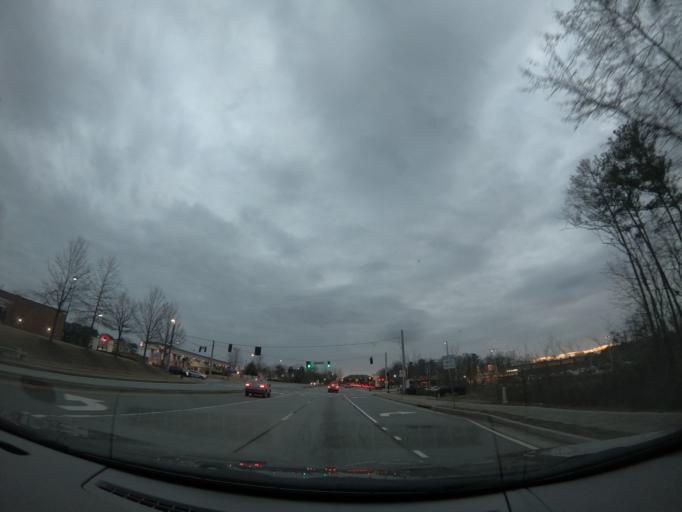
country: US
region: Georgia
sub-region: Fulton County
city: Roswell
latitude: 34.0406
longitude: -84.3467
